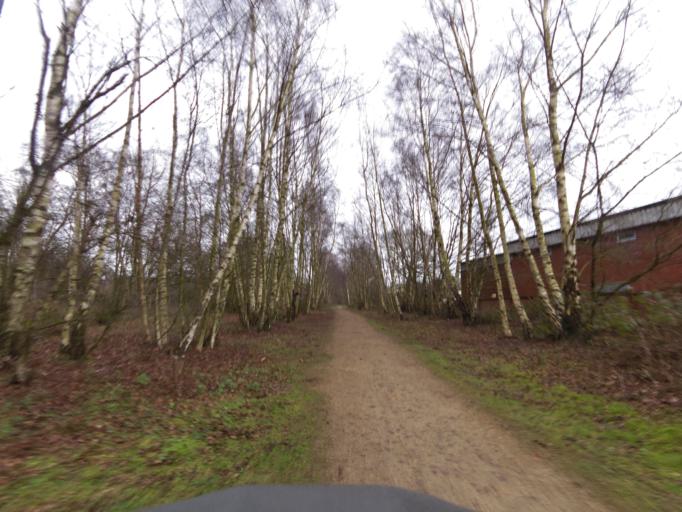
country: GB
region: England
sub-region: Norfolk
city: Mattishall
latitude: 52.7222
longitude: 1.1169
